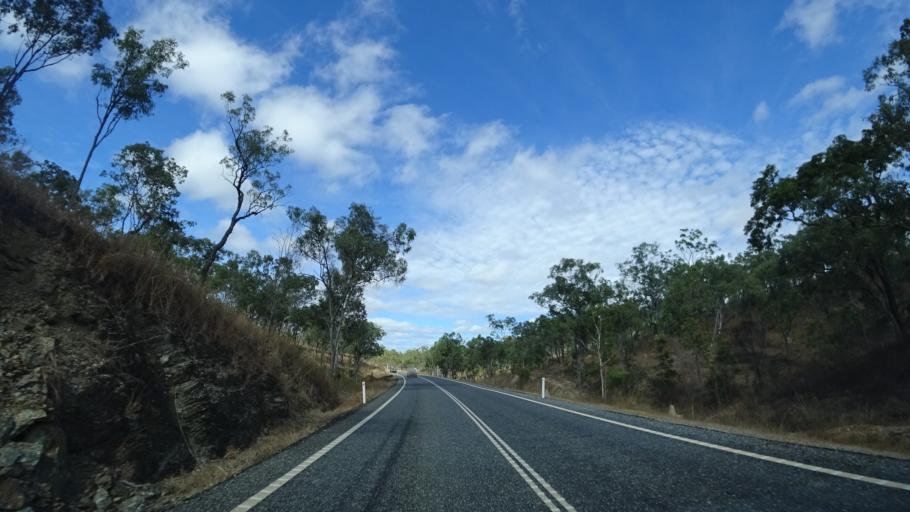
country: AU
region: Queensland
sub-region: Cairns
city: Port Douglas
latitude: -16.2758
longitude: 144.7138
